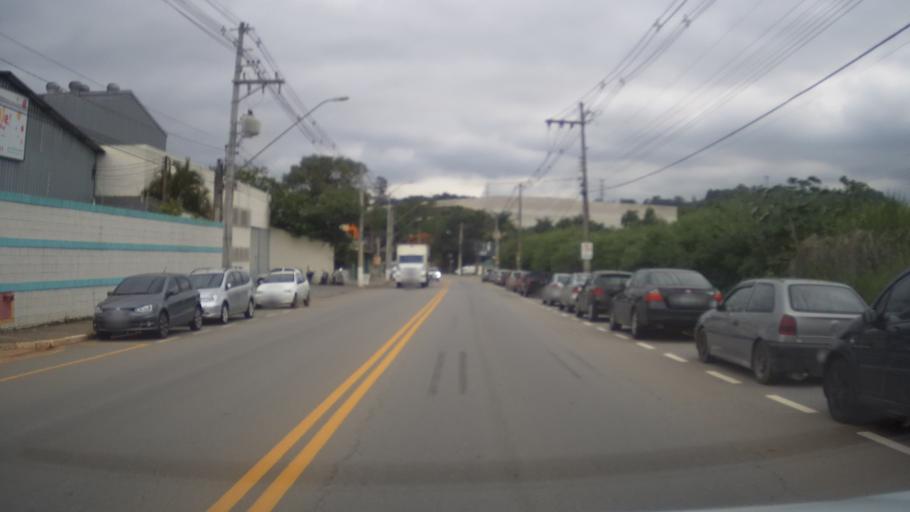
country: BR
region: Sao Paulo
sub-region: Louveira
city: Louveira
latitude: -23.0956
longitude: -46.9487
